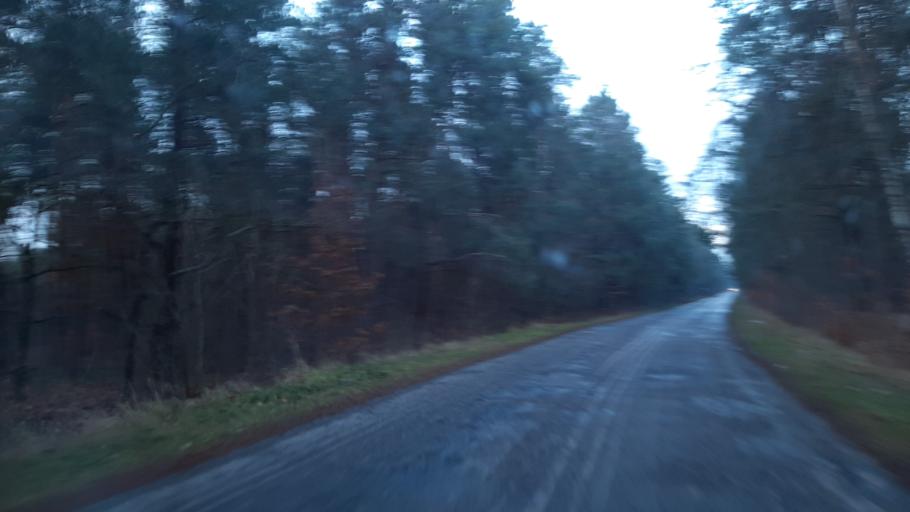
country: PL
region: Lublin Voivodeship
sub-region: Powiat lubartowski
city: Kamionka
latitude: 51.4794
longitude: 22.4699
